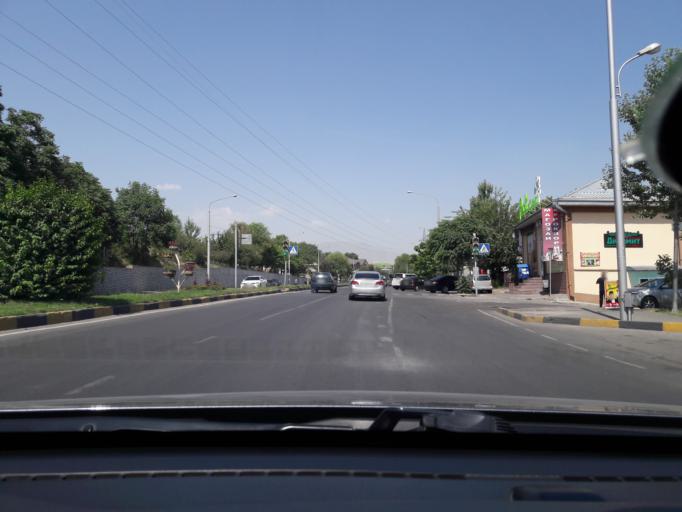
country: TJ
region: Dushanbe
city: Dushanbe
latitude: 38.5929
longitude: 68.7443
